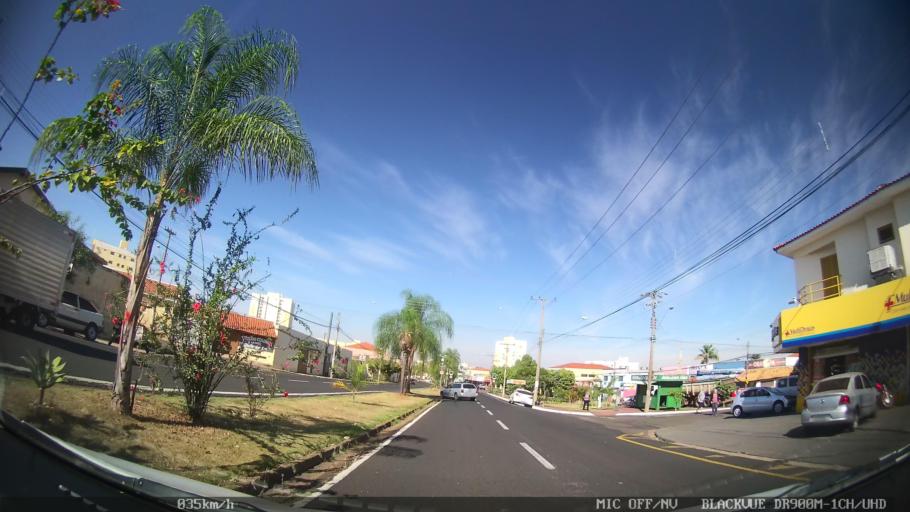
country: BR
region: Sao Paulo
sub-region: Sao Jose Do Rio Preto
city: Sao Jose do Rio Preto
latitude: -20.7826
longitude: -49.3685
